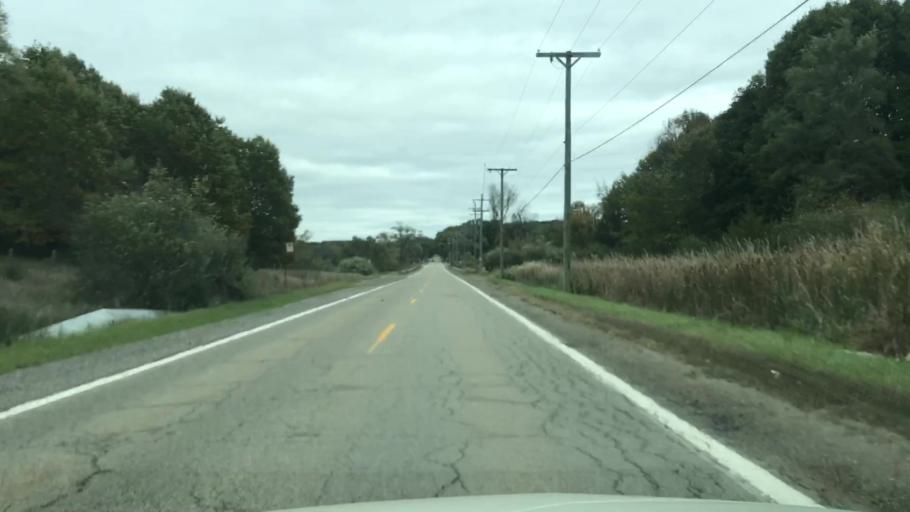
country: US
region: Michigan
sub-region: Macomb County
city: Shelby
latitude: 42.7419
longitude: -83.0723
